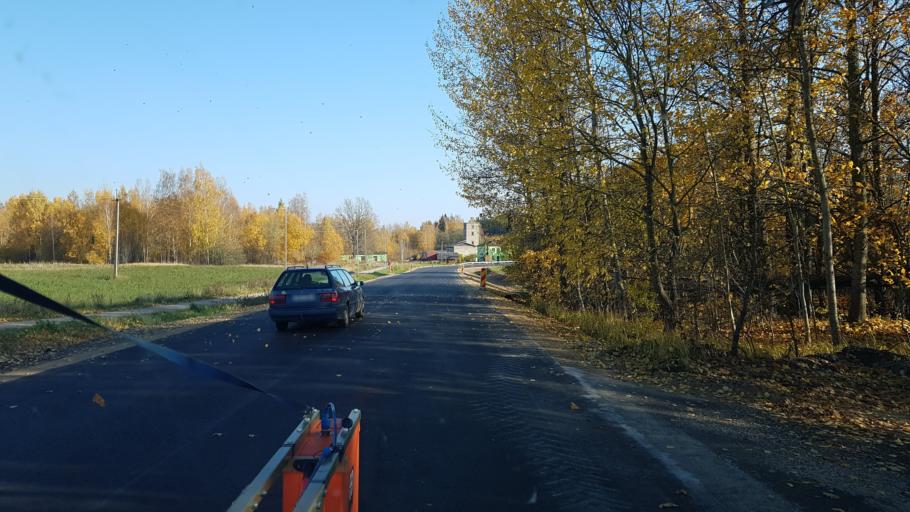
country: EE
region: Vorumaa
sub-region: Antsla vald
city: Vana-Antsla
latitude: 57.8374
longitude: 26.5015
